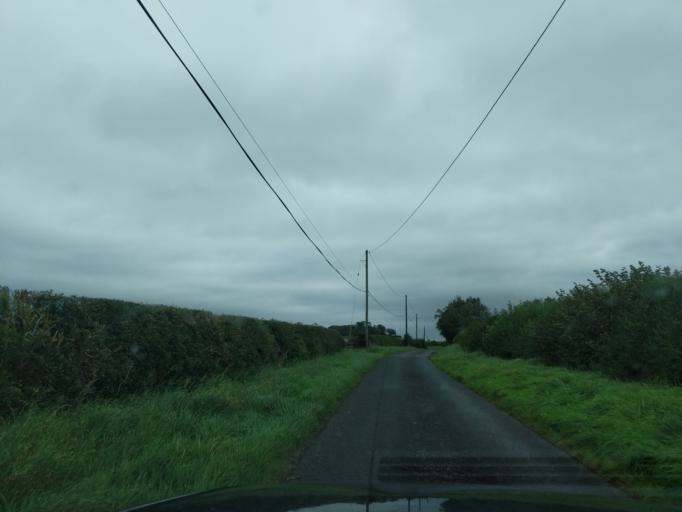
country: GB
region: Scotland
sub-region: The Scottish Borders
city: Kelso
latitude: 55.5916
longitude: -2.5238
